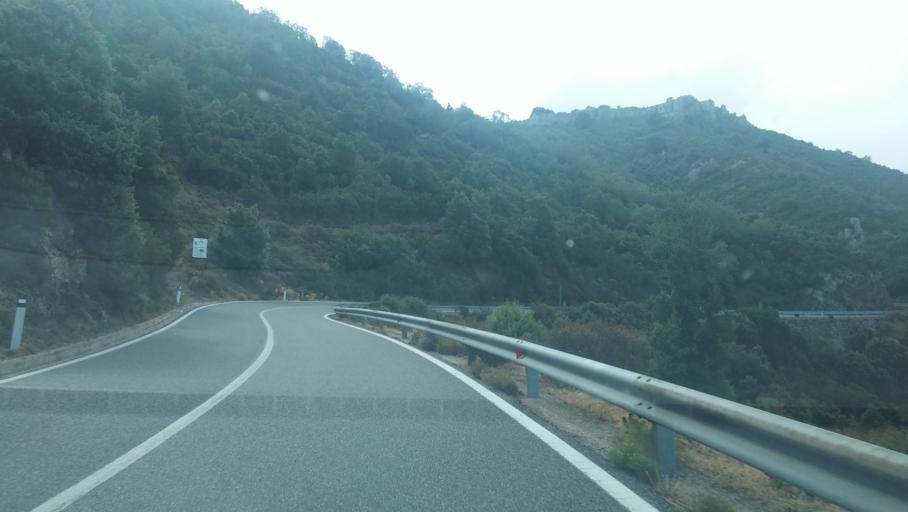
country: IT
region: Sardinia
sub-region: Provincia di Ogliastra
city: Urzulei
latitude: 40.1887
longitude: 9.5356
